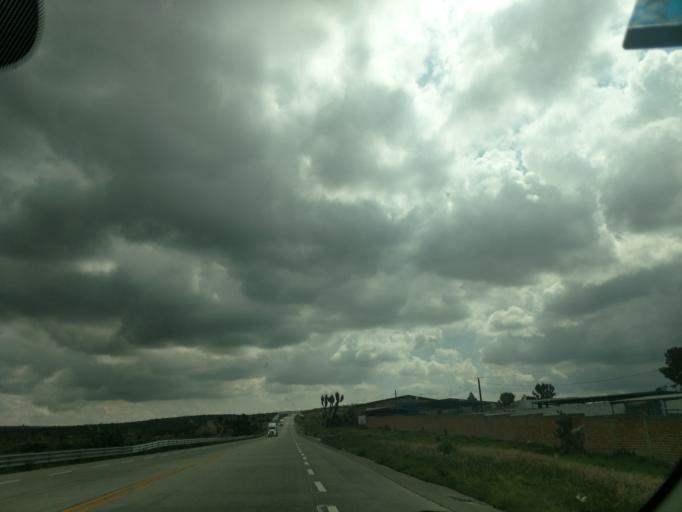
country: MX
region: Jalisco
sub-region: Ojuelos de Jalisco
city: Matanzas
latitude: 21.5648
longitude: -101.6816
